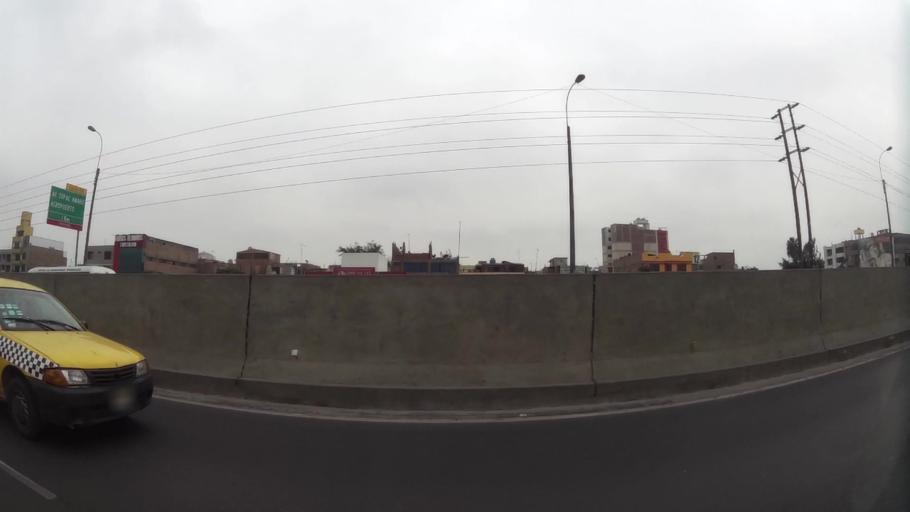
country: PE
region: Lima
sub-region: Lima
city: Independencia
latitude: -11.9671
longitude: -77.0676
